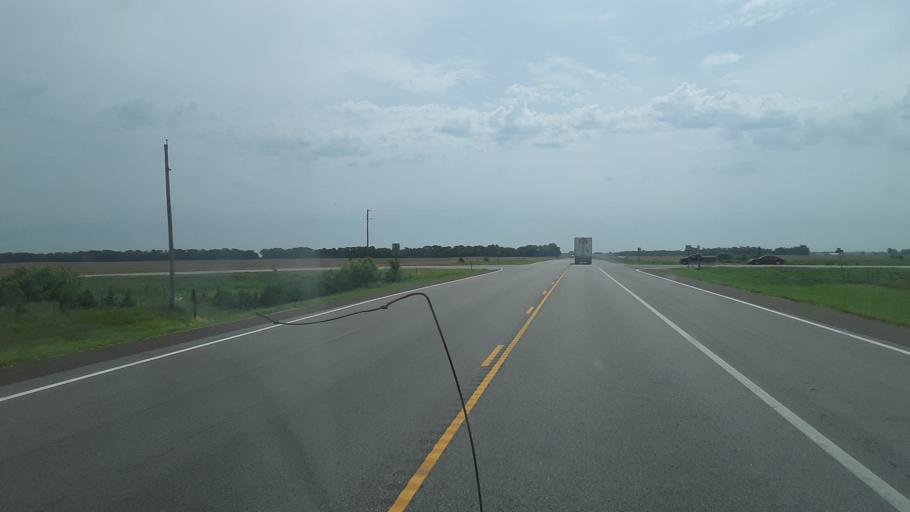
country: US
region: Kansas
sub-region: Reno County
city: Nickerson
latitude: 37.9849
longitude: -98.1799
